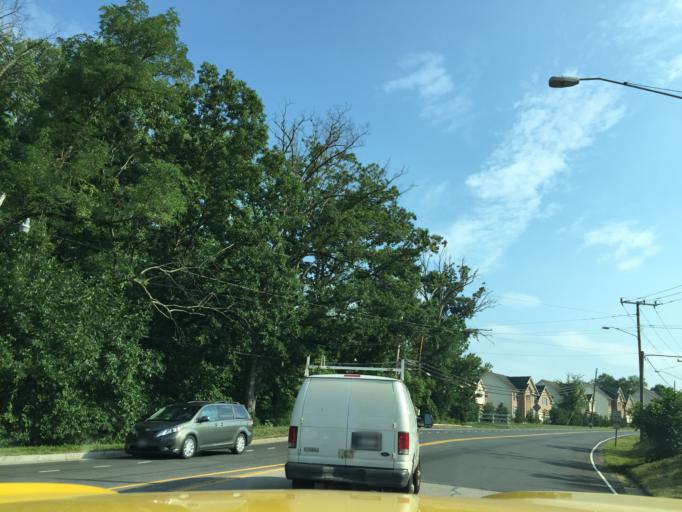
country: US
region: Virginia
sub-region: Fairfax County
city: Hybla Valley
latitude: 38.7389
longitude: -77.0890
